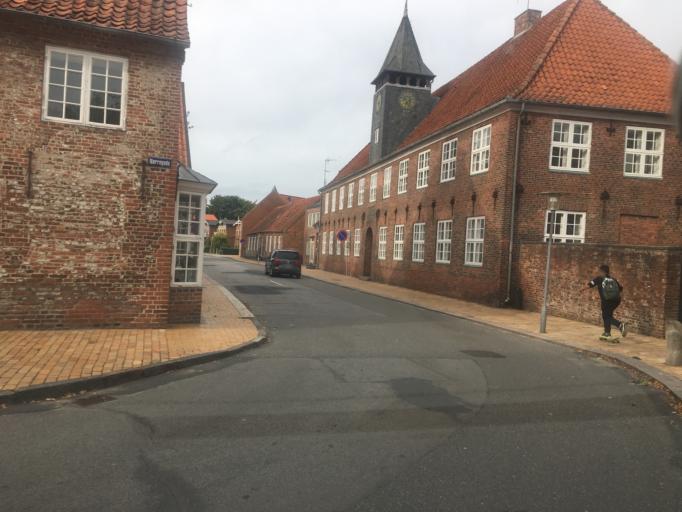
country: DK
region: South Denmark
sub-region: Tonder Kommune
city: Tonder
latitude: 54.9379
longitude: 8.8741
